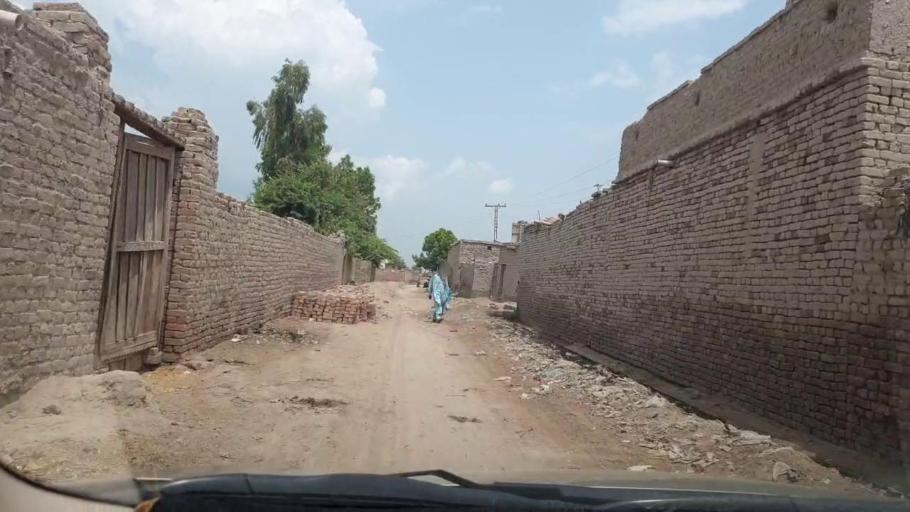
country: PK
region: Sindh
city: Larkana
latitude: 27.5650
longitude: 68.1256
